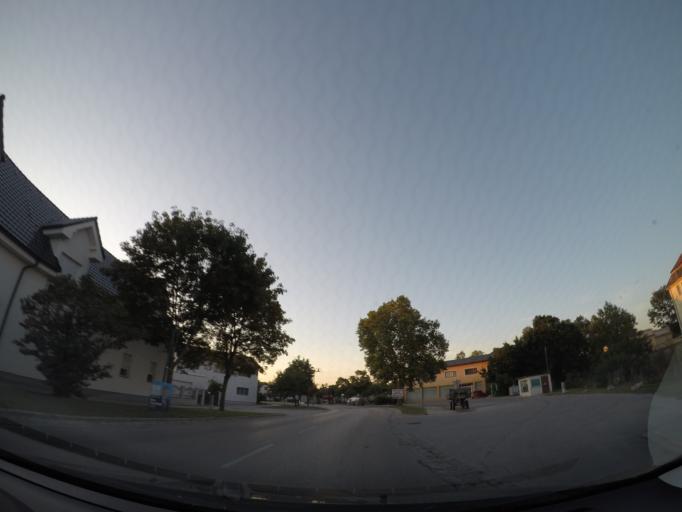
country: AT
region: Lower Austria
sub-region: Politischer Bezirk Baden
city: Seibersdorf
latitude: 47.9589
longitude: 16.5188
